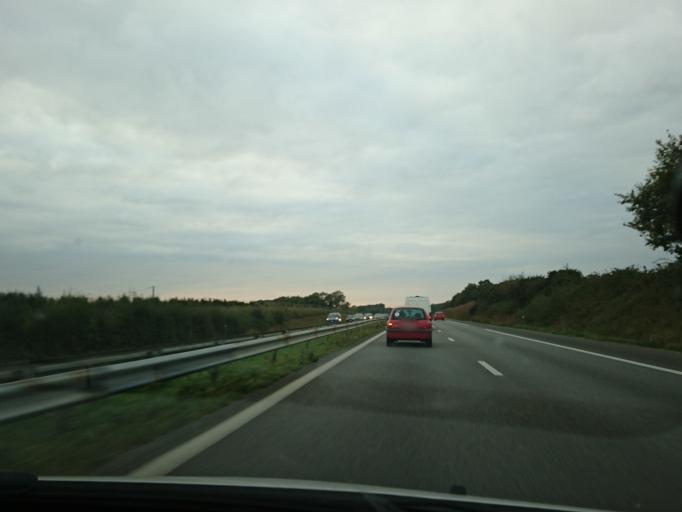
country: FR
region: Brittany
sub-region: Departement du Morbihan
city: Ploeren
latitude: 47.6613
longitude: -2.8335
